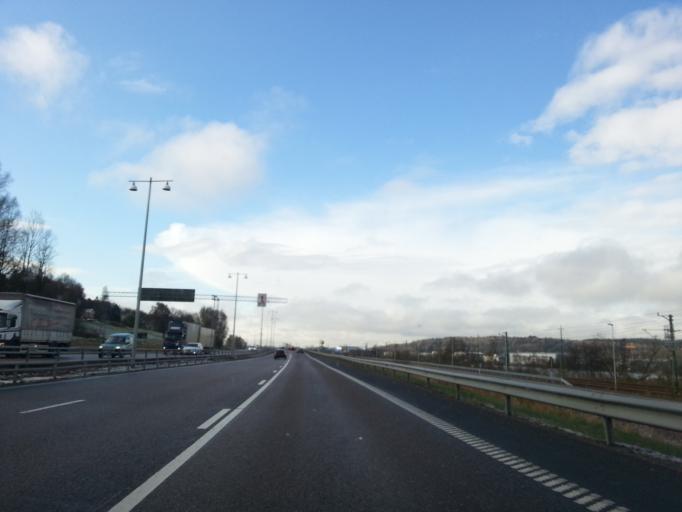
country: SE
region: Vaestra Goetaland
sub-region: Goteborg
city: Hammarkullen
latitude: 57.7845
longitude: 12.0092
